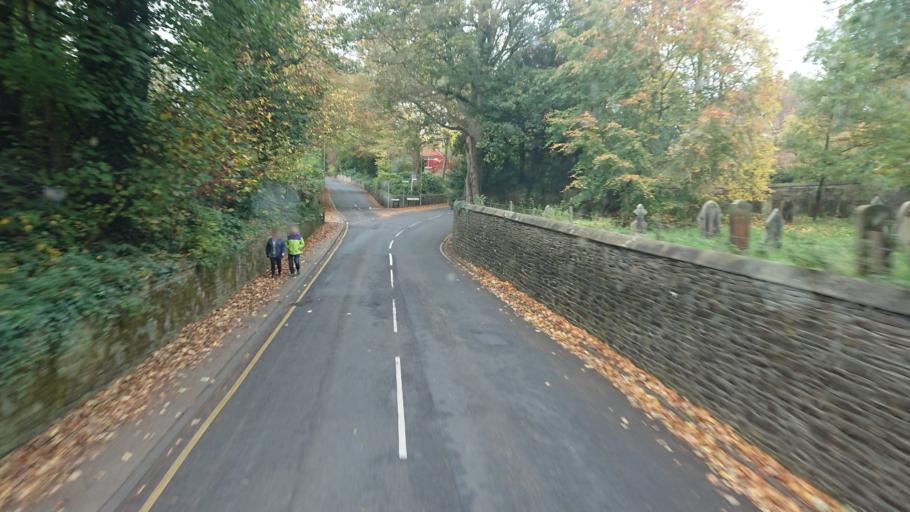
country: GB
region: England
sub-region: North Yorkshire
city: Skipton
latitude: 53.9646
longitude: -2.0205
